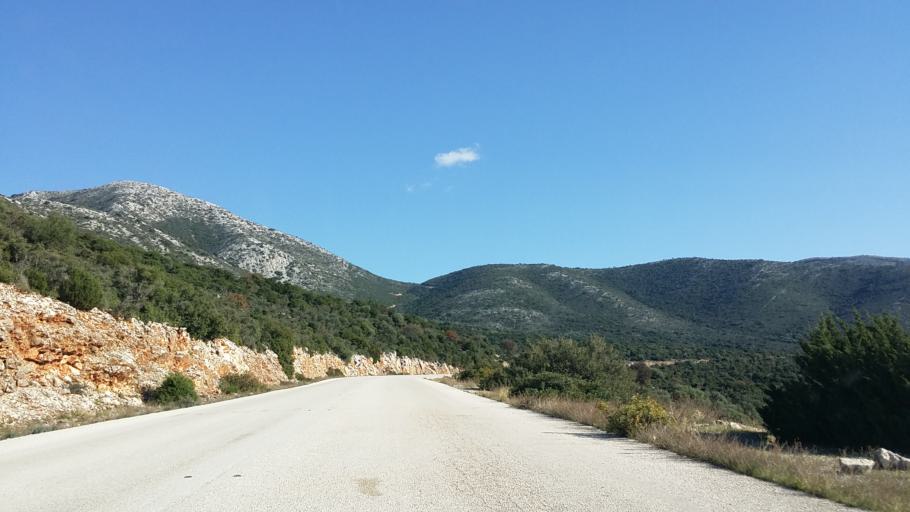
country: GR
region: West Greece
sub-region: Nomos Aitolias kai Akarnanias
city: Astakos
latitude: 38.5418
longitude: 21.0235
